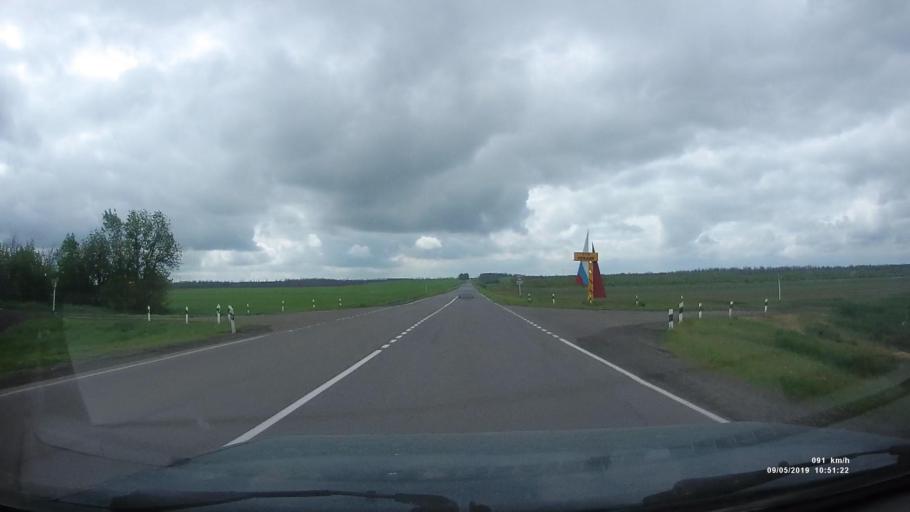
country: RU
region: Rostov
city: Peshkovo
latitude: 46.9159
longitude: 39.3552
